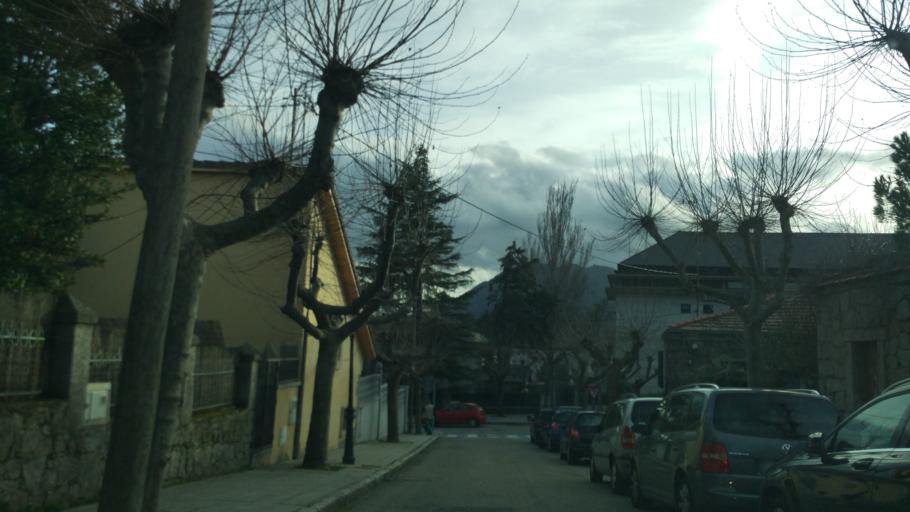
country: ES
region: Madrid
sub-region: Provincia de Madrid
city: El Escorial
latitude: 40.5819
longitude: -4.1289
